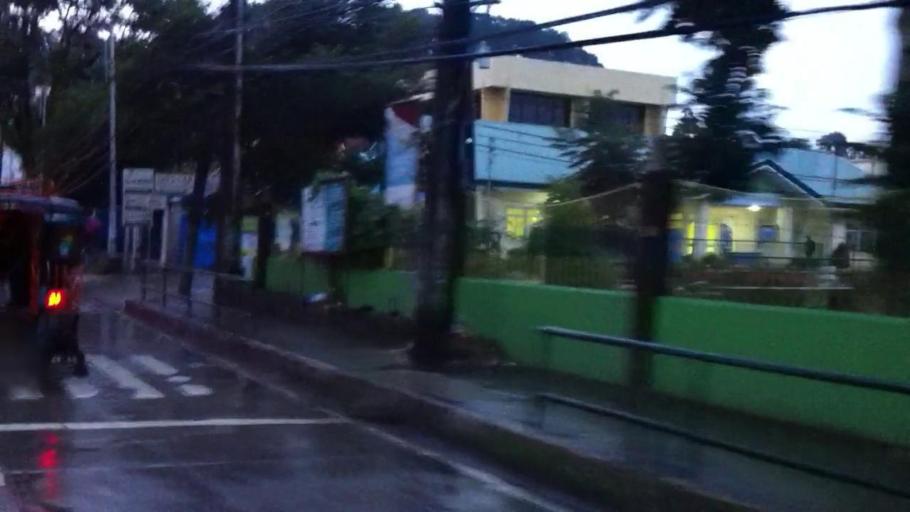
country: PH
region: Cordillera
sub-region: Province of Benguet
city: La Trinidad
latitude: 16.4602
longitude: 120.5884
